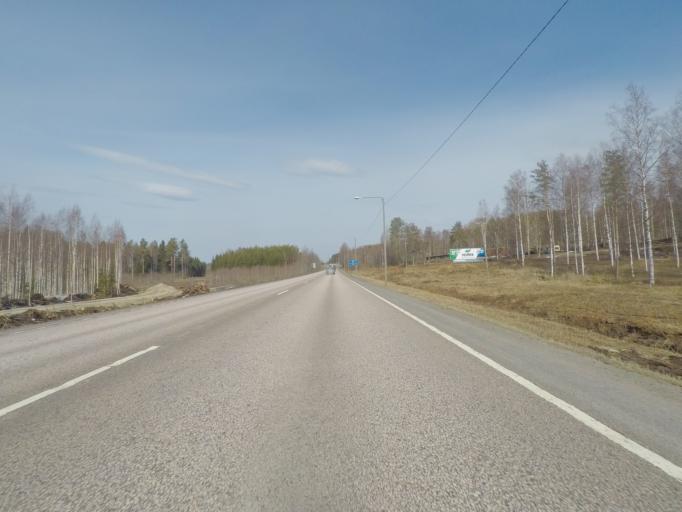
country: FI
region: Central Finland
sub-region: Joutsa
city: Leivonmaeki
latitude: 61.9138
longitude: 26.1168
